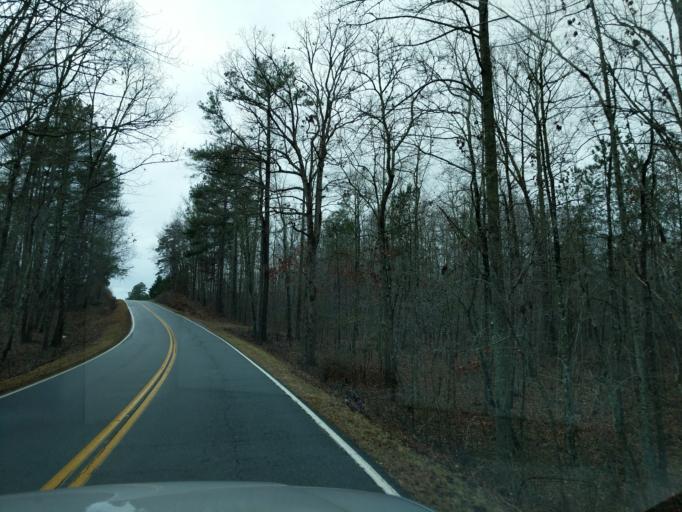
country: US
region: South Carolina
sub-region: Oconee County
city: Walhalla
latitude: 34.8004
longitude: -83.1583
